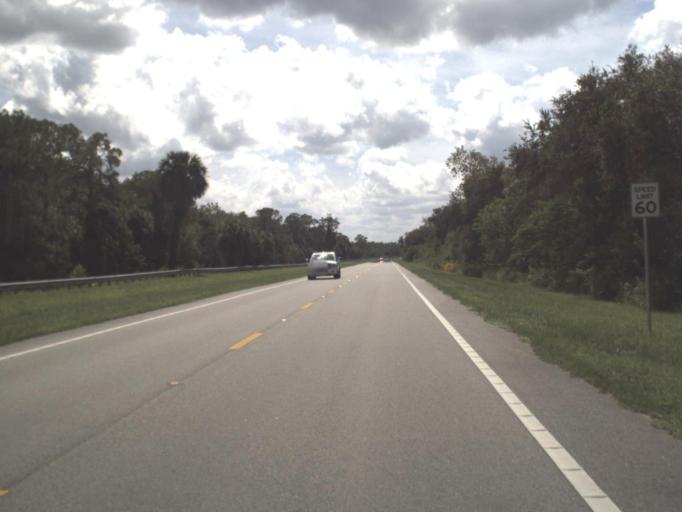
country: US
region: Florida
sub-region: Collier County
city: Immokalee
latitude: 26.2570
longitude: -81.3419
